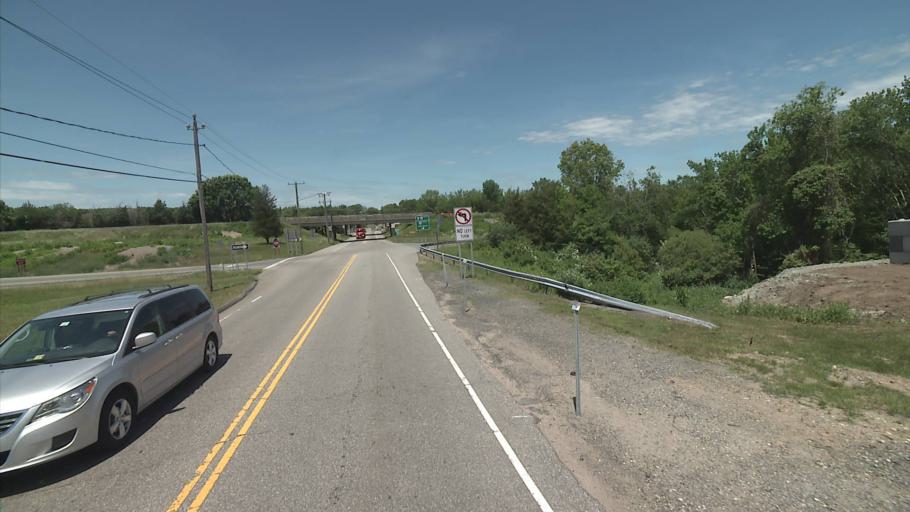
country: US
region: Rhode Island
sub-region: Washington County
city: Ashaway
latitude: 41.4392
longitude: -71.7986
